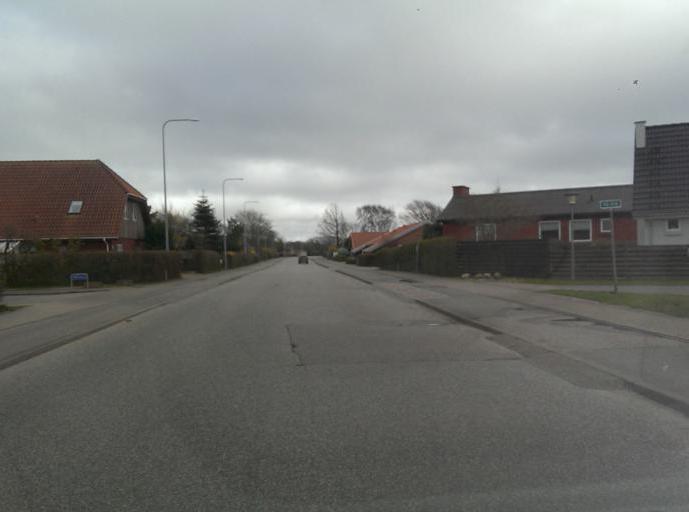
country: DK
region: South Denmark
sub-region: Esbjerg Kommune
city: Esbjerg
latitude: 55.4855
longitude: 8.4768
